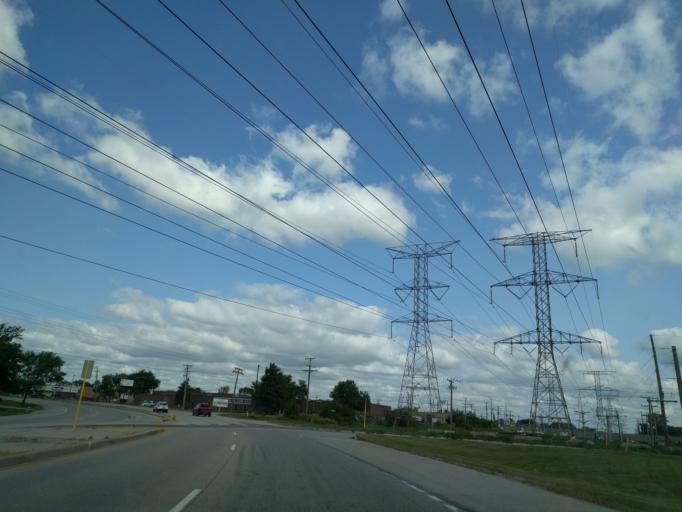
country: US
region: Illinois
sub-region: Cook County
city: Elk Grove Village
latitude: 42.0249
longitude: -87.9642
